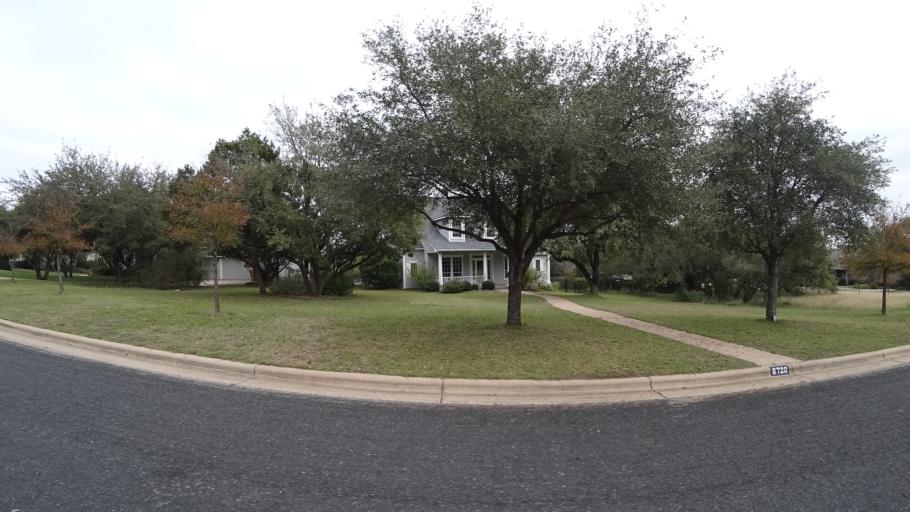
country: US
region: Texas
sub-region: Travis County
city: Shady Hollow
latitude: 30.2207
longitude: -97.8814
